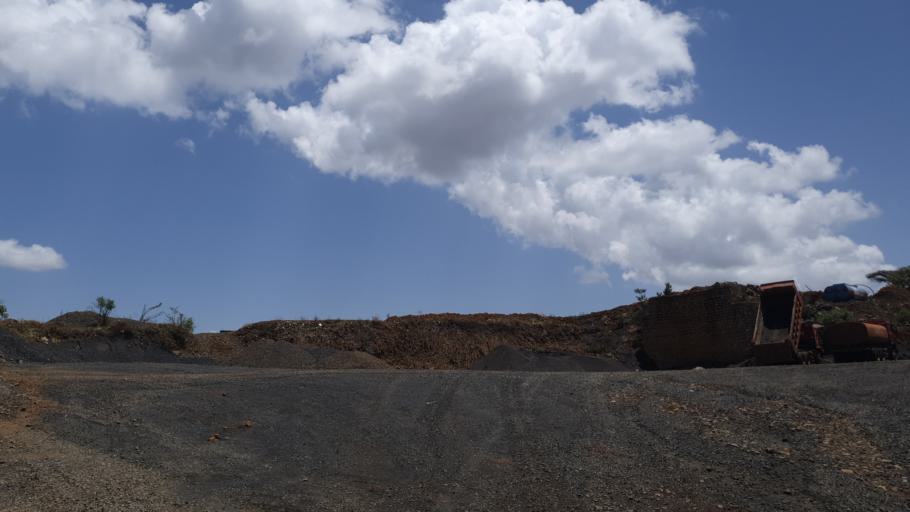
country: ET
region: Oromiya
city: Shambu
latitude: 10.0233
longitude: 36.8833
